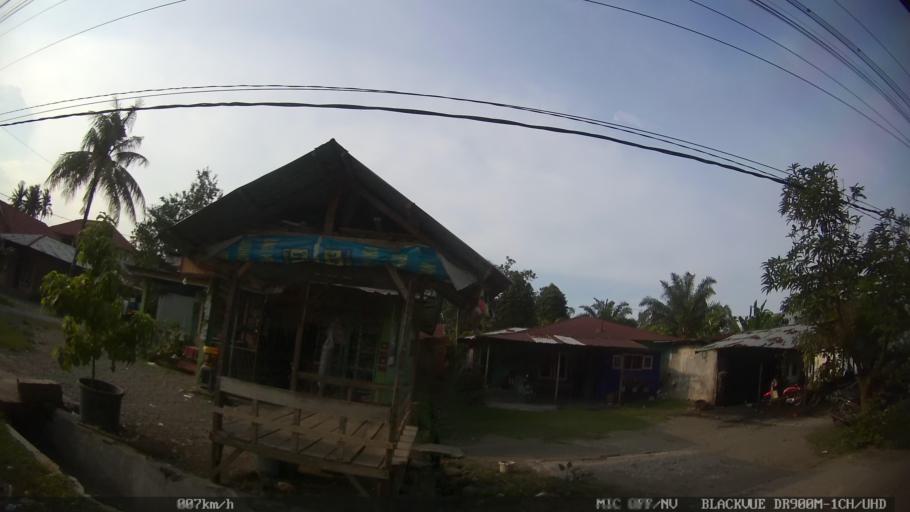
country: ID
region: North Sumatra
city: Binjai
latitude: 3.6173
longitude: 98.5320
